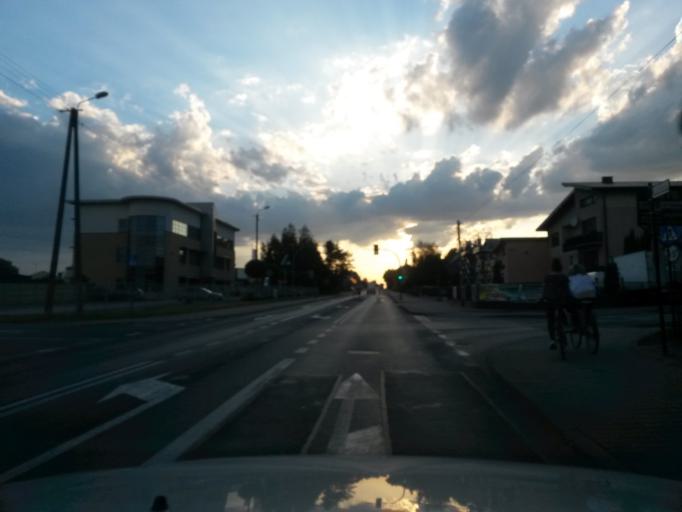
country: PL
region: Lodz Voivodeship
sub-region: Powiat wielunski
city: Wielun
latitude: 51.2270
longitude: 18.5567
